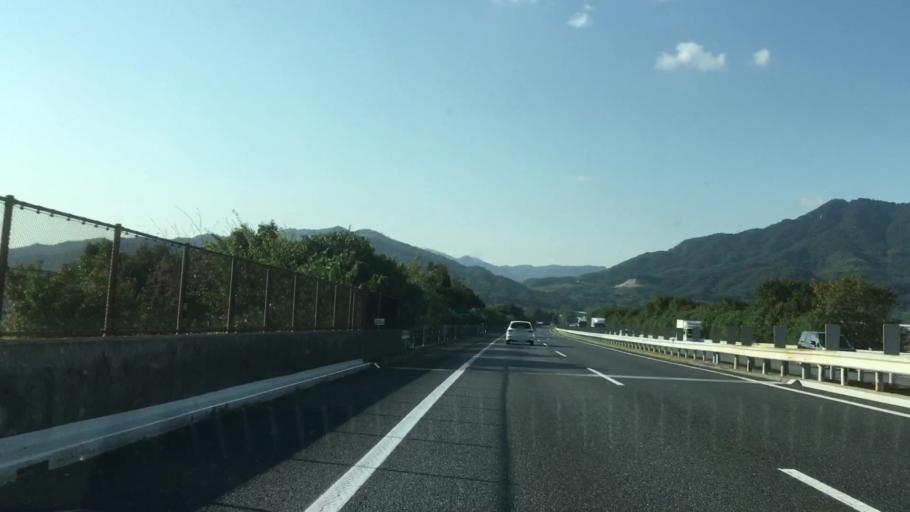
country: JP
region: Yamaguchi
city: Hofu
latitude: 34.0608
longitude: 131.6105
